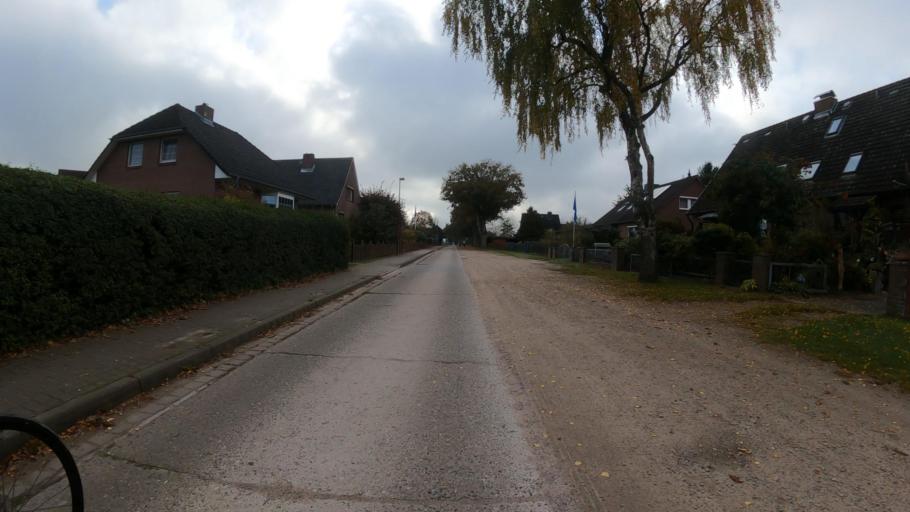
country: DE
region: Lower Saxony
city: Neu Wulmstorf
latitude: 53.4364
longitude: 9.8050
